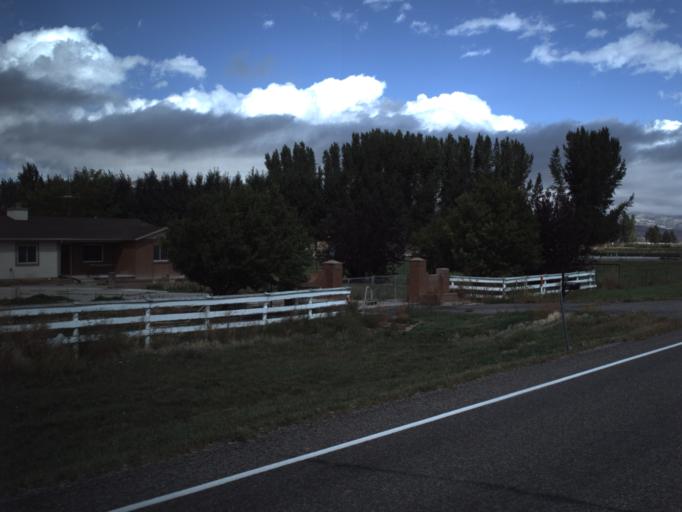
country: US
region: Utah
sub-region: Sevier County
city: Monroe
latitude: 38.6955
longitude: -112.1138
